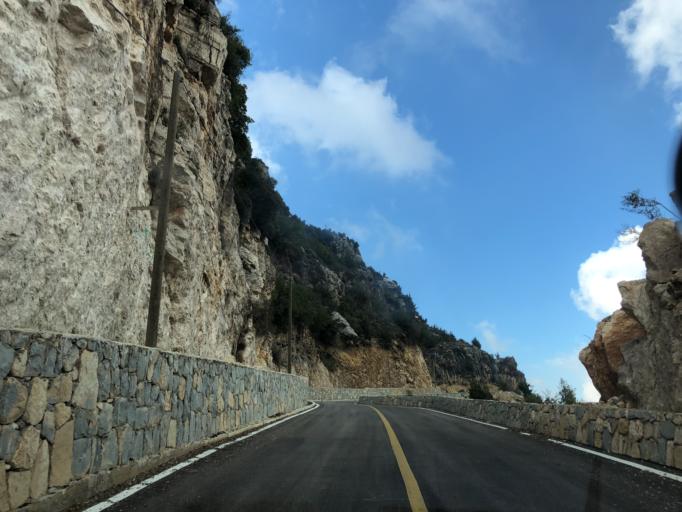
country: LB
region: Liban-Nord
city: Amioun
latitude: 34.2099
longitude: 35.8308
